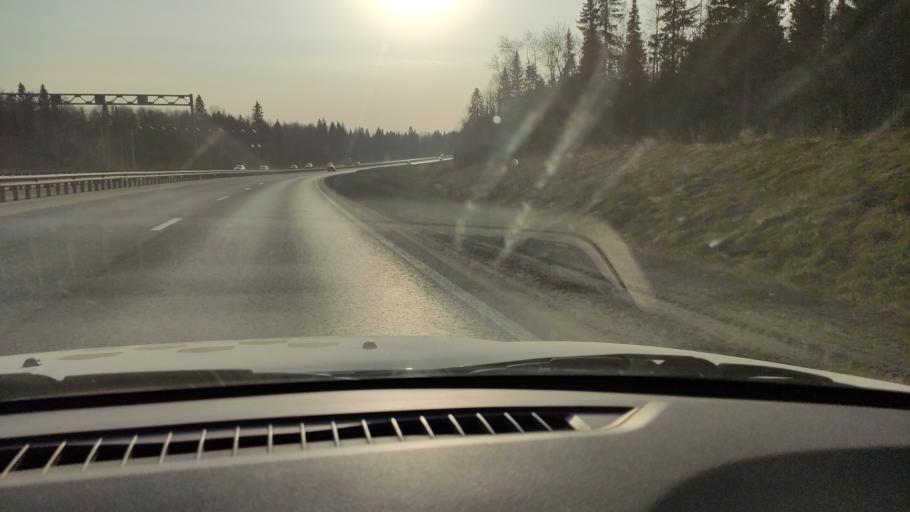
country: RU
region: Perm
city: Novyye Lyady
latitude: 58.0329
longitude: 56.4338
